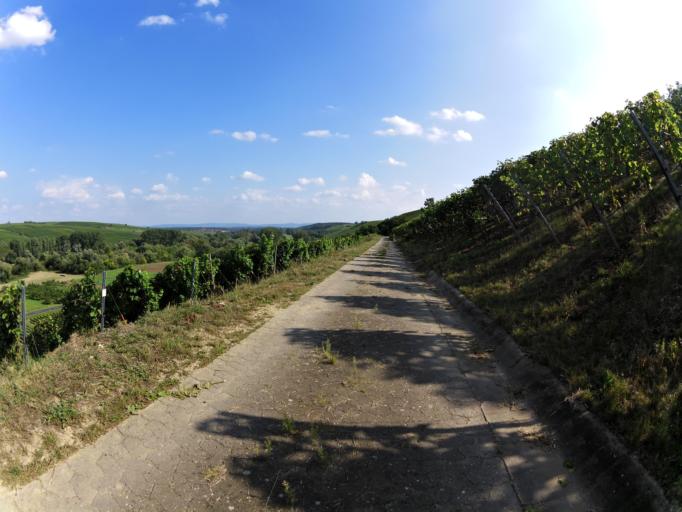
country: DE
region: Bavaria
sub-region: Regierungsbezirk Unterfranken
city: Nordheim
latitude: 49.8408
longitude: 10.1703
